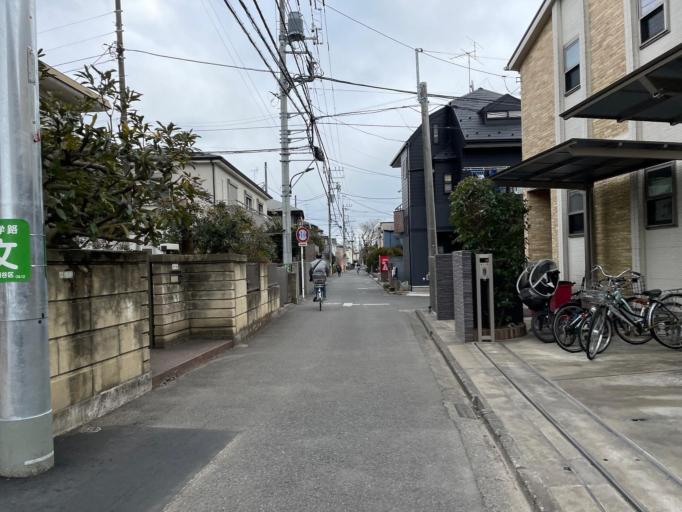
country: JP
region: Tokyo
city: Chofugaoka
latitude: 35.6316
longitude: 139.5931
